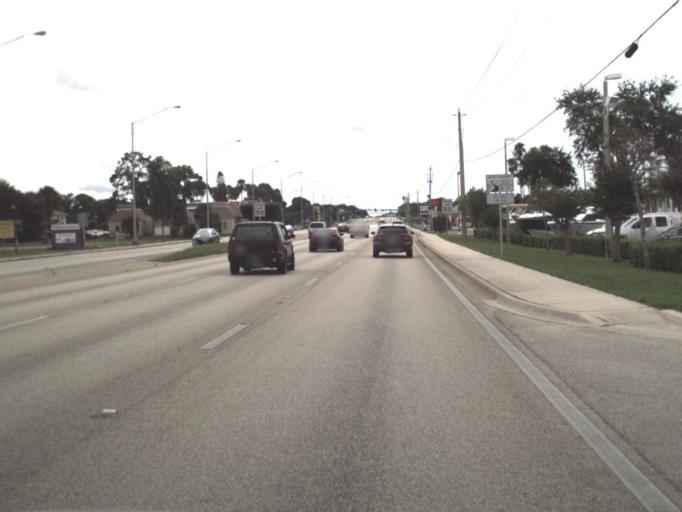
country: US
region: Florida
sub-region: Manatee County
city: Whitfield
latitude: 27.4157
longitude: -82.5744
